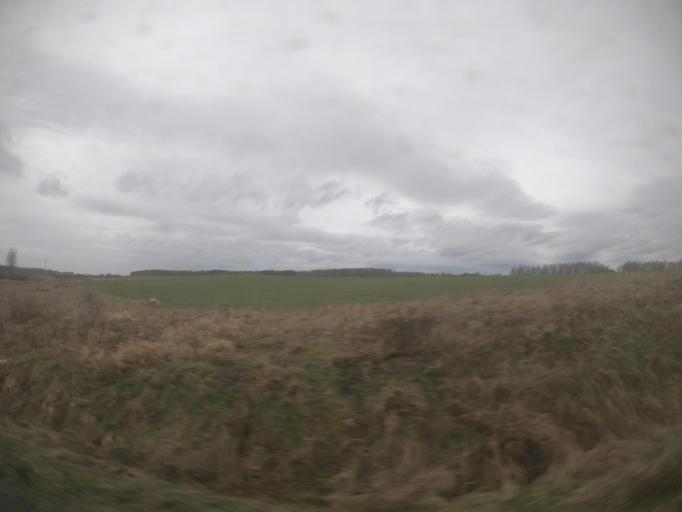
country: PL
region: West Pomeranian Voivodeship
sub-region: Powiat szczecinecki
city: Szczecinek
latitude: 53.7219
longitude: 16.8007
